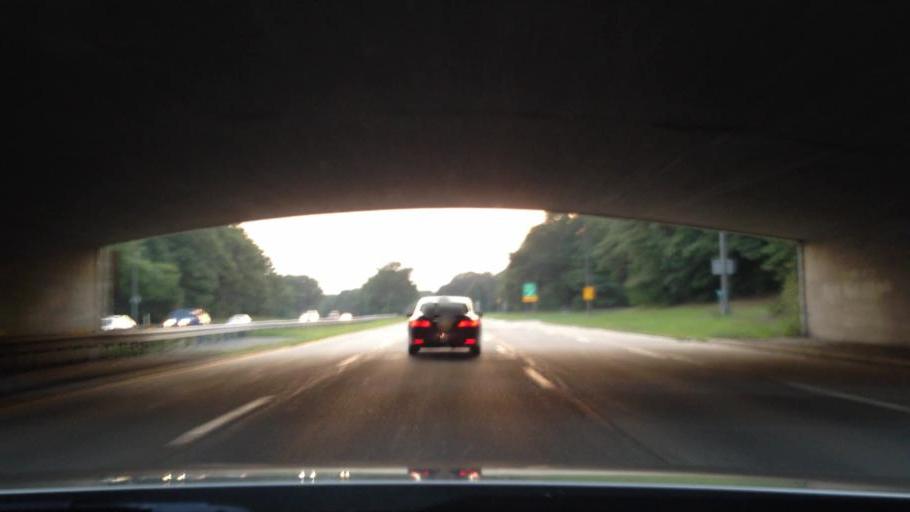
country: US
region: New York
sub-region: Suffolk County
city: Islip Terrace
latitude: 40.7556
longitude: -73.2090
